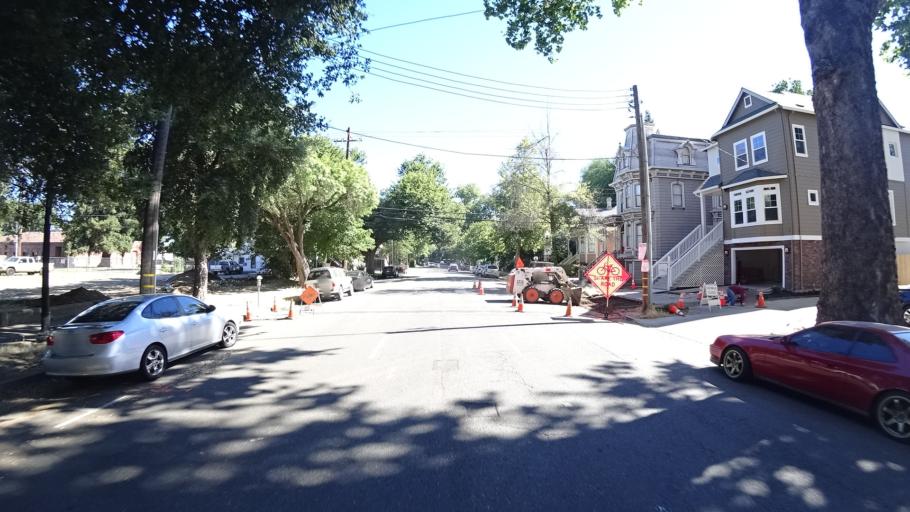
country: US
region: California
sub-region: Sacramento County
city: Sacramento
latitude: 38.5856
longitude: -121.4942
